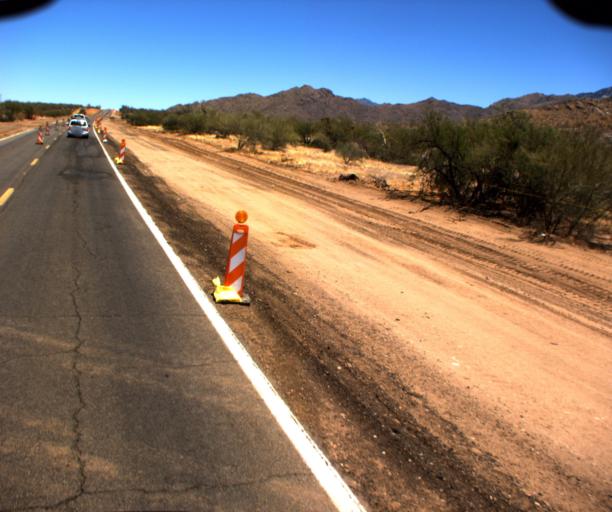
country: US
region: Arizona
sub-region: Pima County
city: Sells
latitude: 31.9941
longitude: -111.7036
